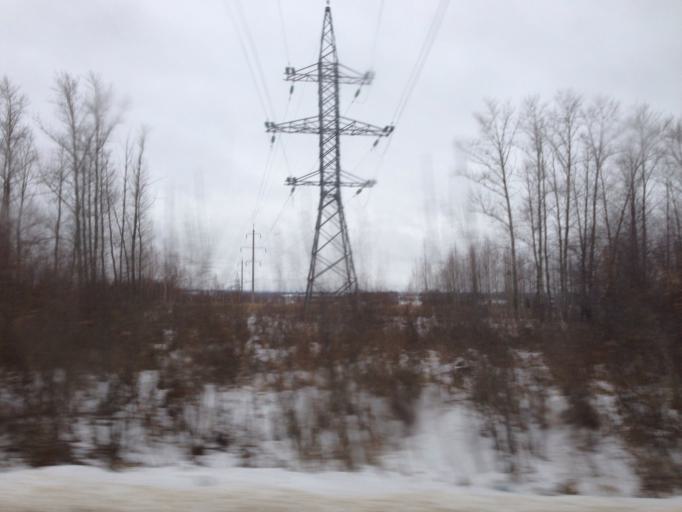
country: RU
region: Tula
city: Uzlovaya
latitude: 54.0012
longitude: 38.1213
